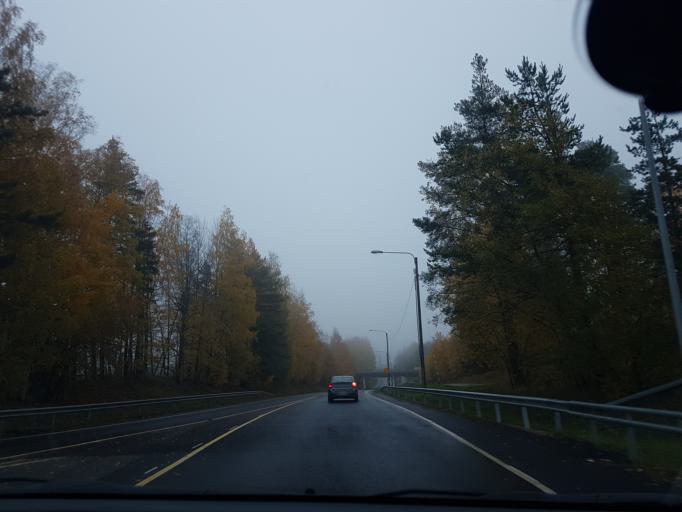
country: FI
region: Uusimaa
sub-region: Helsinki
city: Jaervenpaeae
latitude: 60.4556
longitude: 25.0975
